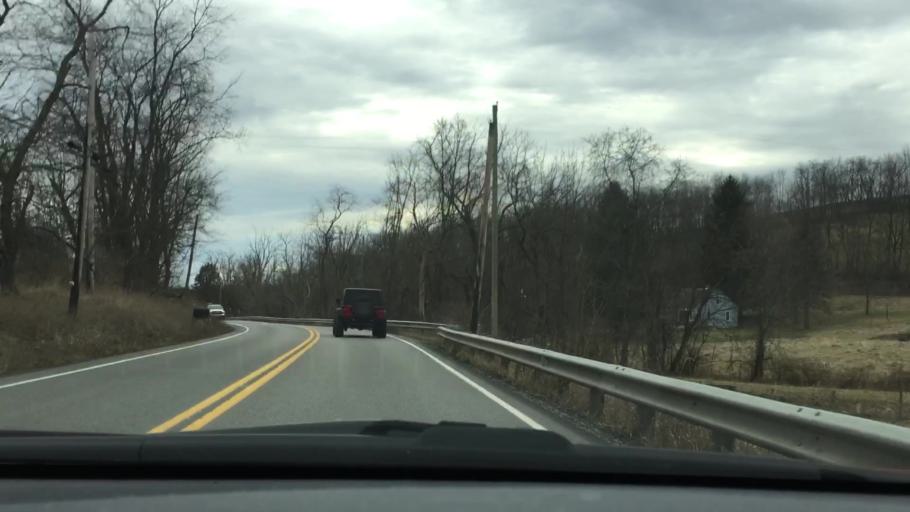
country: US
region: Pennsylvania
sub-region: Washington County
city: Muse
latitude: 40.2967
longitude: -80.2182
